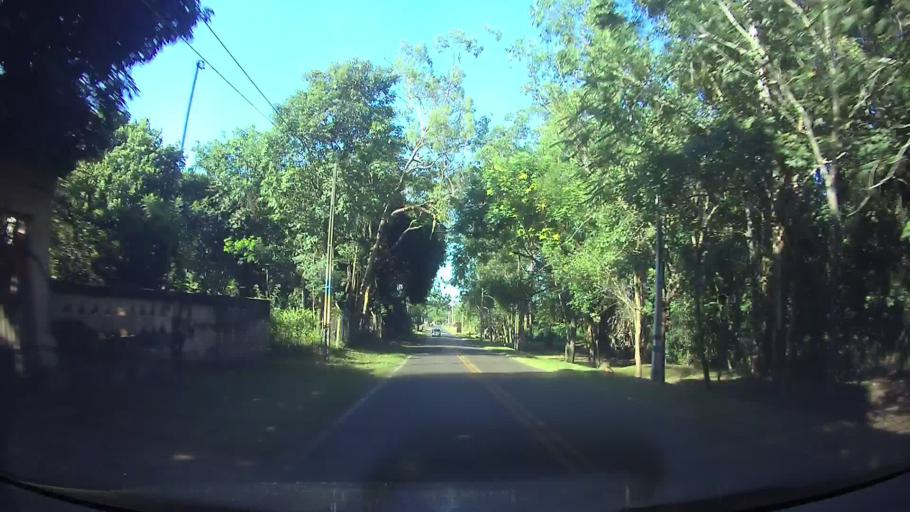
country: PY
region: Cordillera
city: Atyra
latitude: -25.2870
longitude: -57.1785
